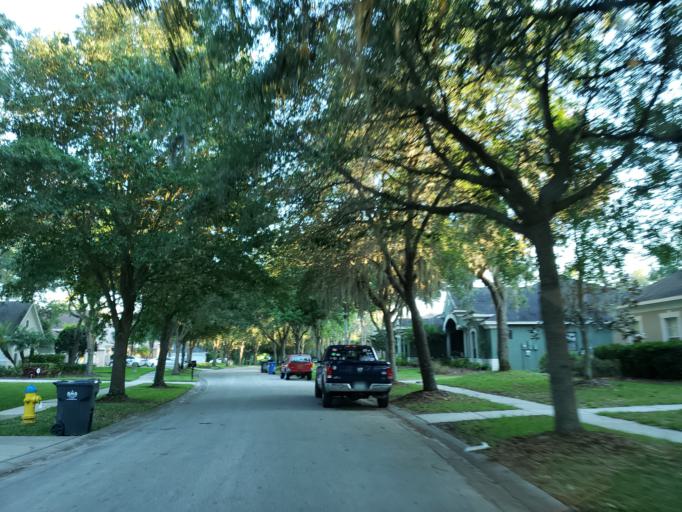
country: US
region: Florida
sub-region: Hillsborough County
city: Fish Hawk
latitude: 27.8365
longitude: -82.2212
